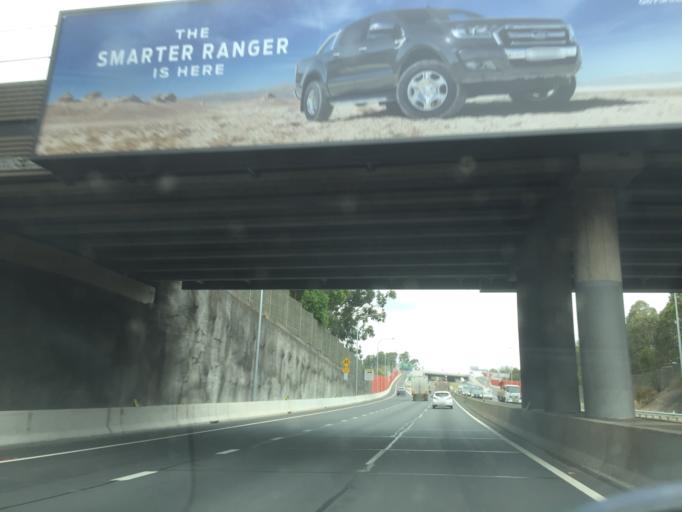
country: AU
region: New South Wales
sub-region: The Hills Shire
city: Baulkham Hills
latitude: -33.7695
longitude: 150.9916
